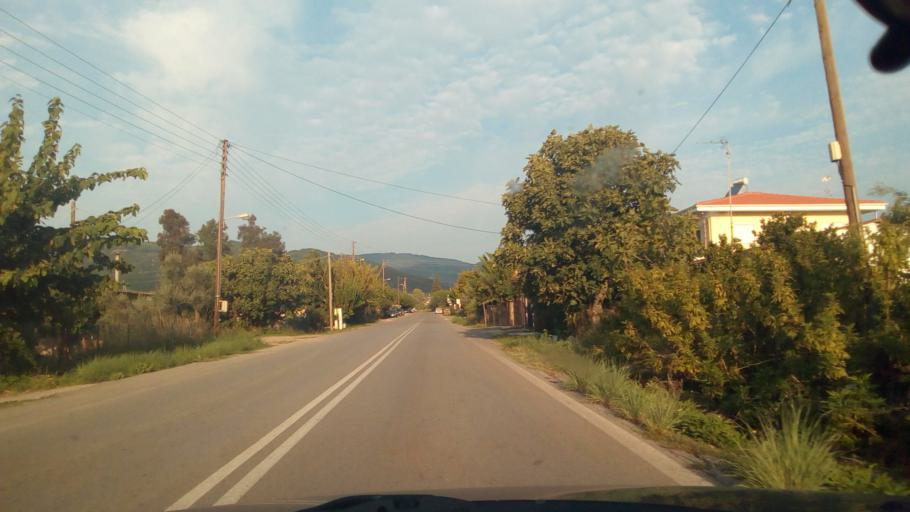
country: GR
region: West Greece
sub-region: Nomos Aitolias kai Akarnanias
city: Nafpaktos
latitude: 38.3953
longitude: 21.8071
